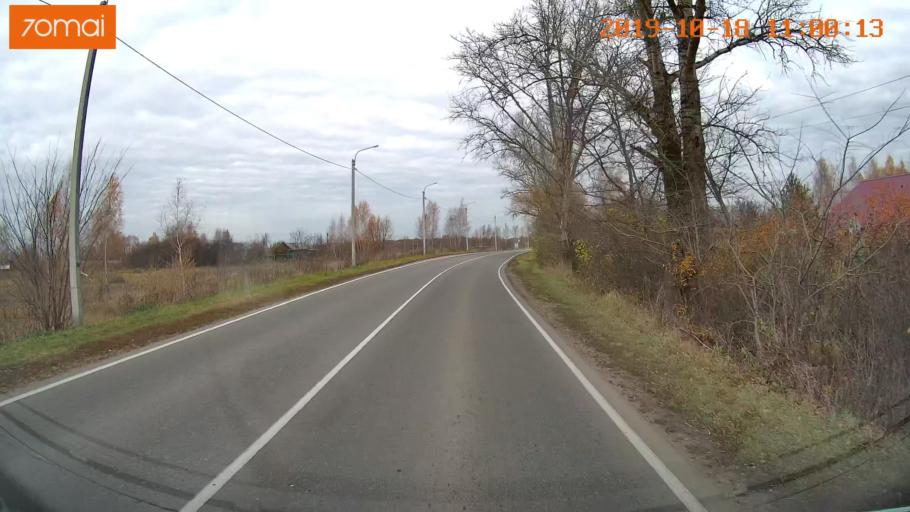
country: RU
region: Tula
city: Yepifan'
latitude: 53.8404
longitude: 38.5529
